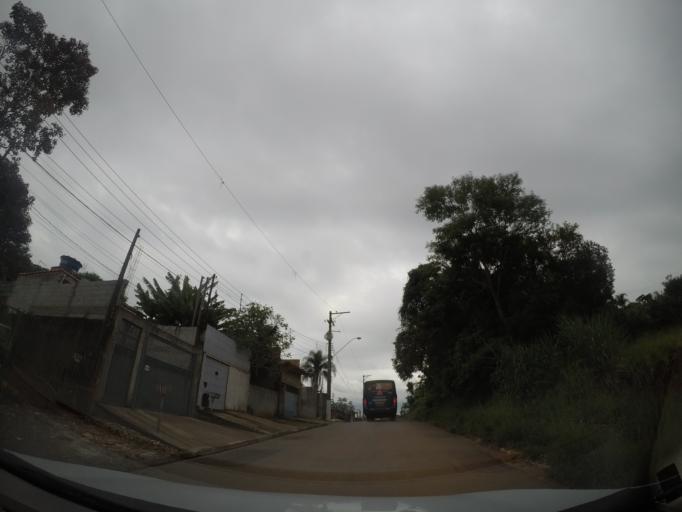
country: BR
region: Sao Paulo
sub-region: Aruja
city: Aruja
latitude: -23.3812
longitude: -46.3990
